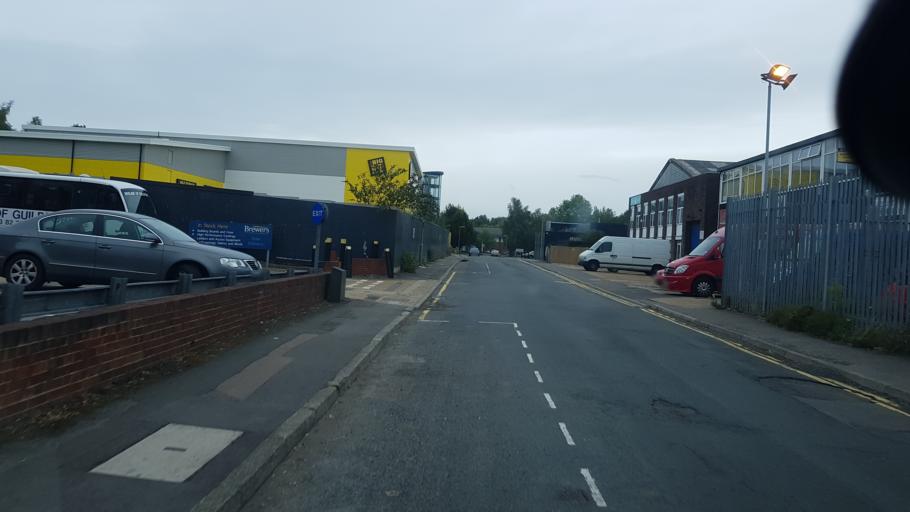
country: GB
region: England
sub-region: Surrey
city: Guildford
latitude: 51.2458
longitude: -0.5828
